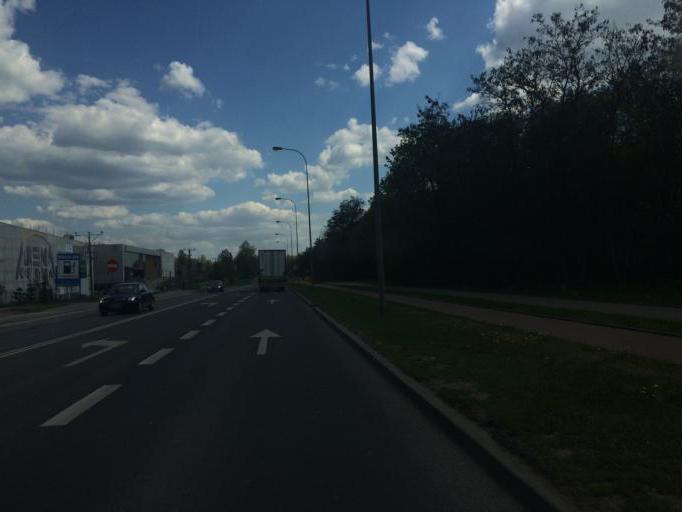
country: PL
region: Warmian-Masurian Voivodeship
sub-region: Powiat ostrodzki
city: Ostroda
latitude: 53.6853
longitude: 19.9902
